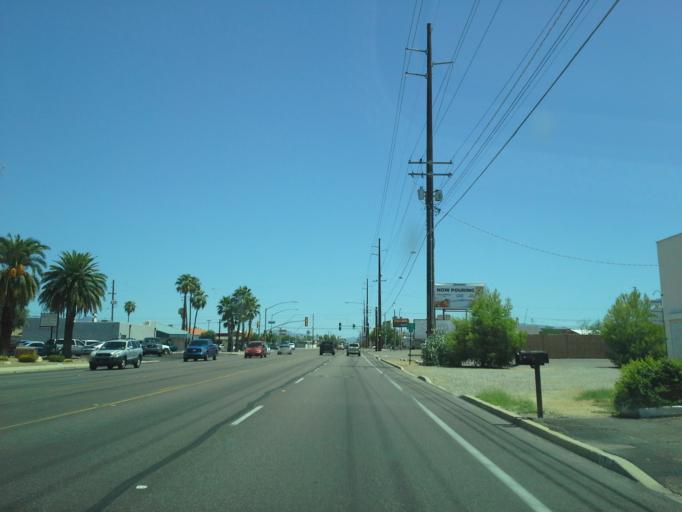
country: US
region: Arizona
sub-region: Pima County
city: Catalina Foothills
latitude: 32.2648
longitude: -110.9629
